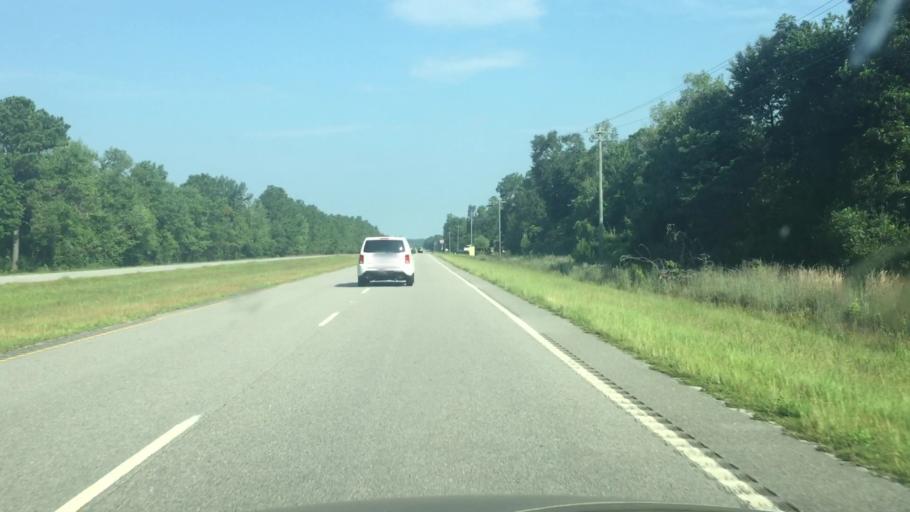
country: US
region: South Carolina
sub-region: Horry County
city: Loris
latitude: 34.0529
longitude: -78.8395
